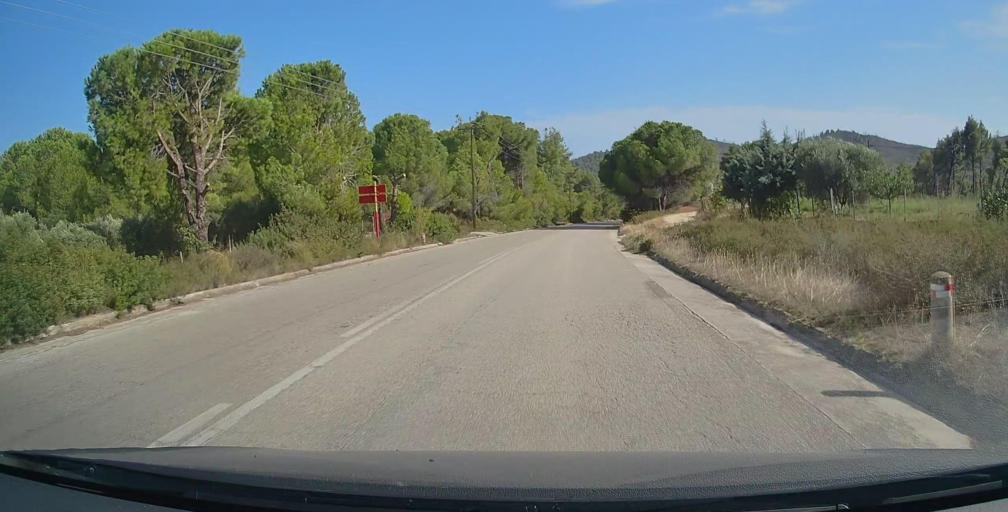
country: GR
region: Central Macedonia
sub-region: Nomos Chalkidikis
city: Sarti
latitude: 40.1233
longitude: 23.9678
